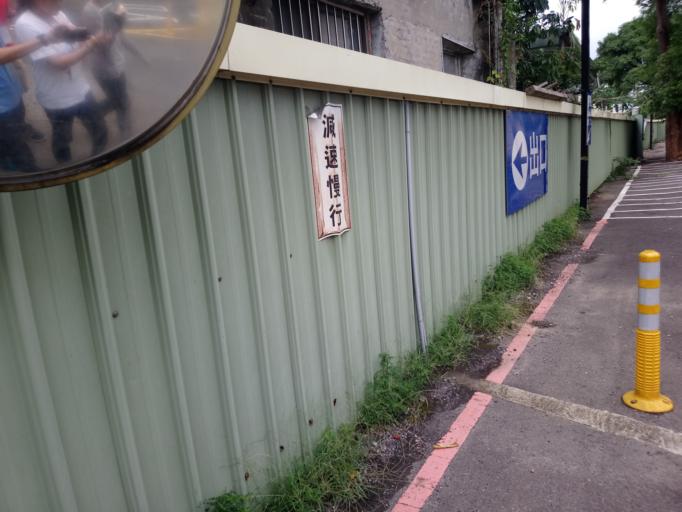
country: TW
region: Taiwan
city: Taoyuan City
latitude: 24.9475
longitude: 121.2459
